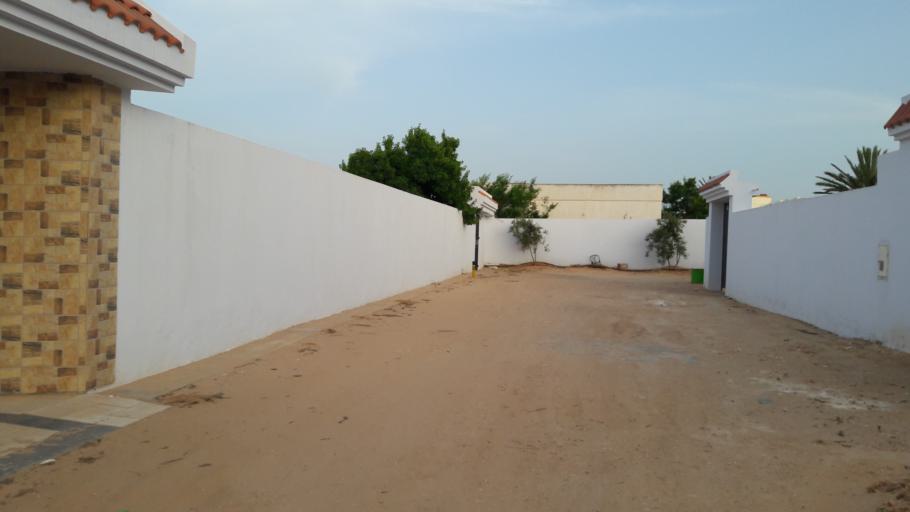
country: TN
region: Safaqis
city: Al Qarmadah
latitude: 34.8141
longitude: 10.7481
